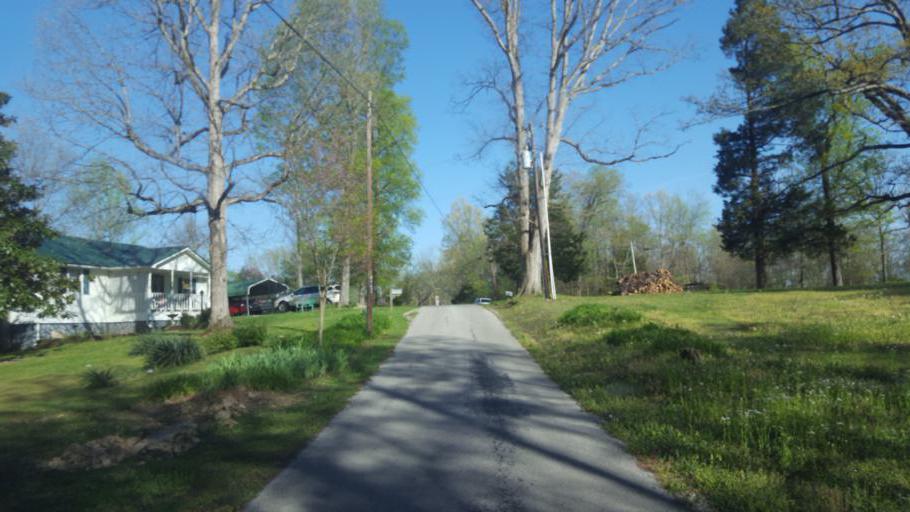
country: US
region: Kentucky
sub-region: Barren County
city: Cave City
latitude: 37.1761
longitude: -86.0321
